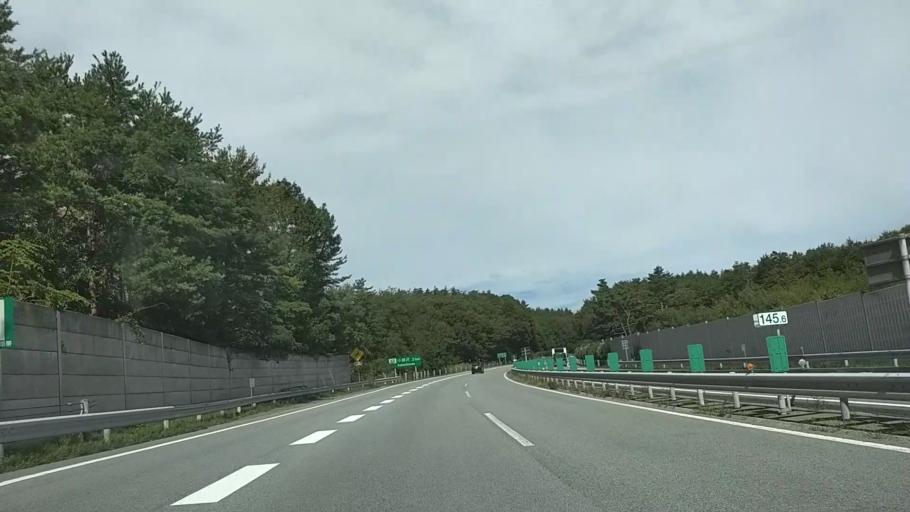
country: JP
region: Yamanashi
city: Nirasaki
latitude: 35.8554
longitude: 138.3348
